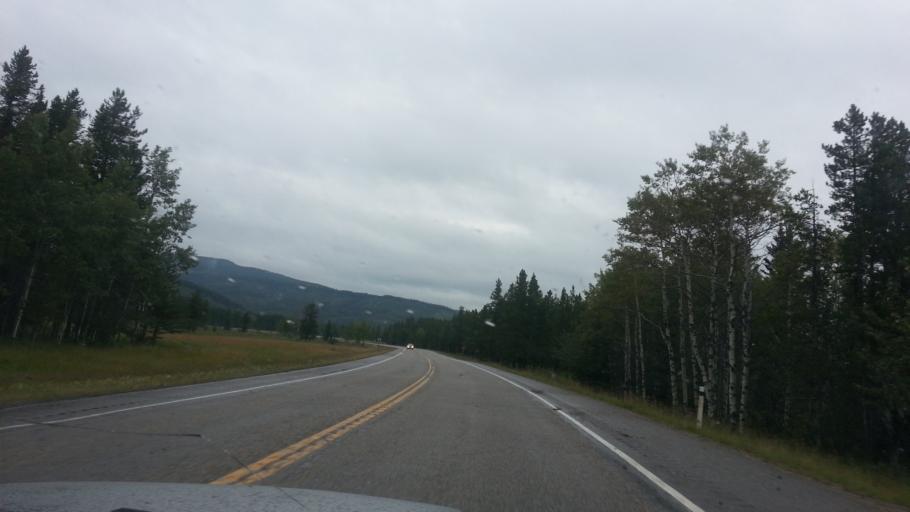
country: CA
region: Alberta
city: Cochrane
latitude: 50.8884
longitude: -114.7054
